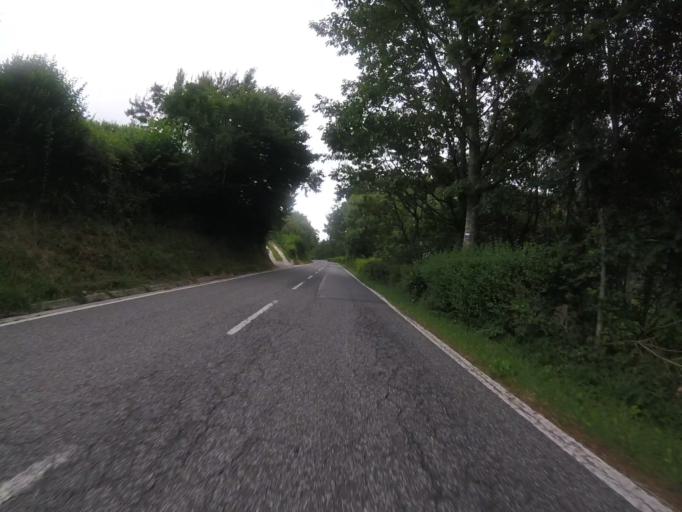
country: ES
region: Navarre
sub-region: Provincia de Navarra
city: Ezkurra
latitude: 43.0826
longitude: -1.8396
